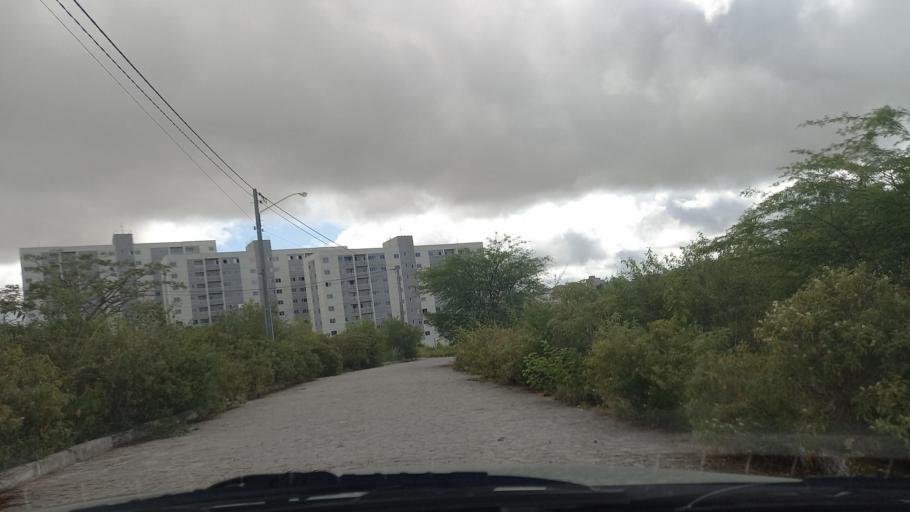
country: BR
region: Pernambuco
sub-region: Caruaru
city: Caruaru
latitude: -8.3054
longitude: -35.9599
